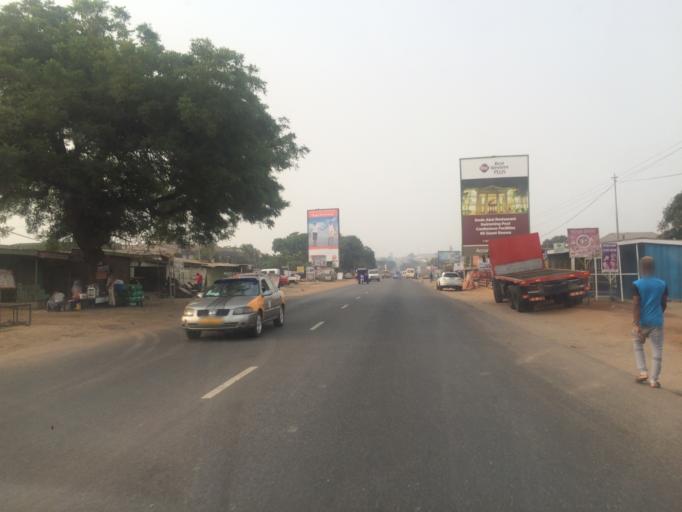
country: GH
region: Greater Accra
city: Nungua
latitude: 5.6124
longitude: -0.0747
